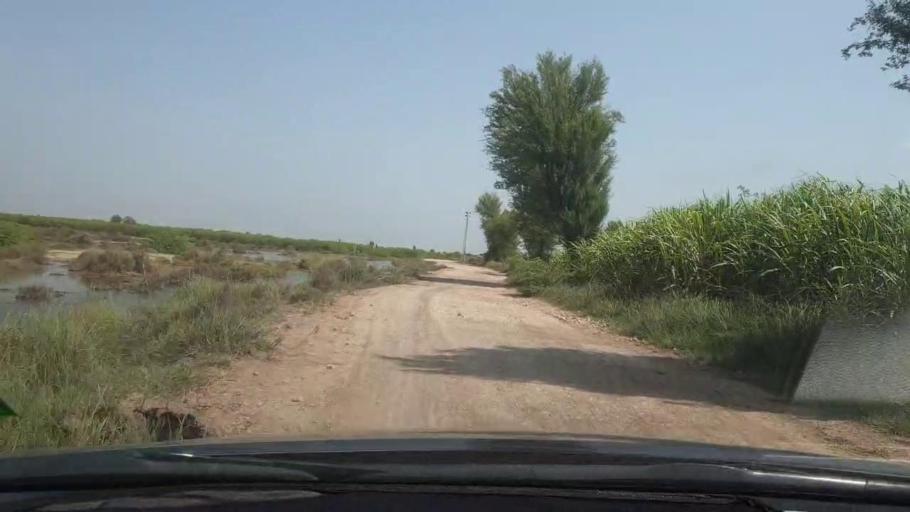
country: PK
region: Sindh
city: Tando Bago
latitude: 24.7825
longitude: 69.1798
